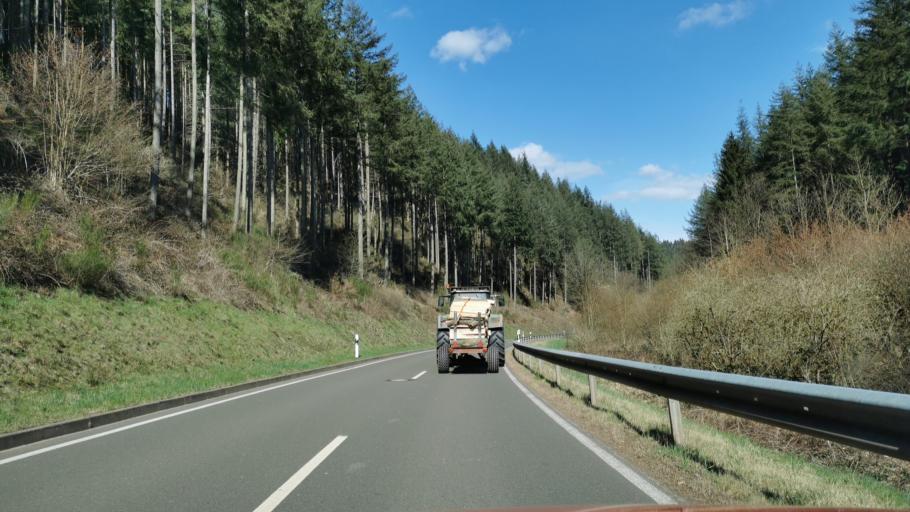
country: DE
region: Rheinland-Pfalz
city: Bruch
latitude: 49.9410
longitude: 6.7823
